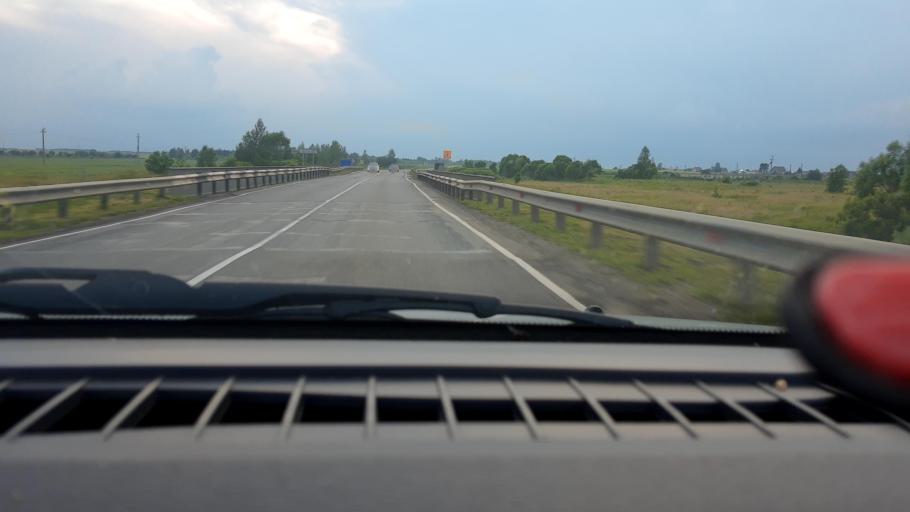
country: RU
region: Nizjnij Novgorod
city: Shatki
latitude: 55.2448
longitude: 44.0122
